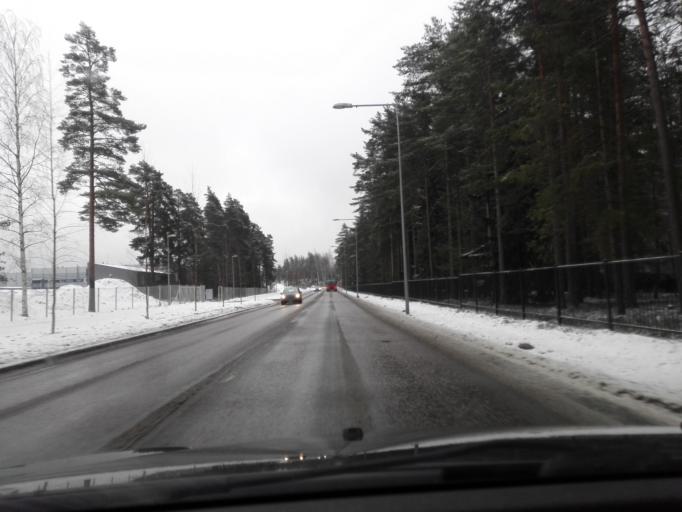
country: FI
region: Uusimaa
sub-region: Helsinki
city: Vantaa
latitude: 60.2941
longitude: 25.0865
